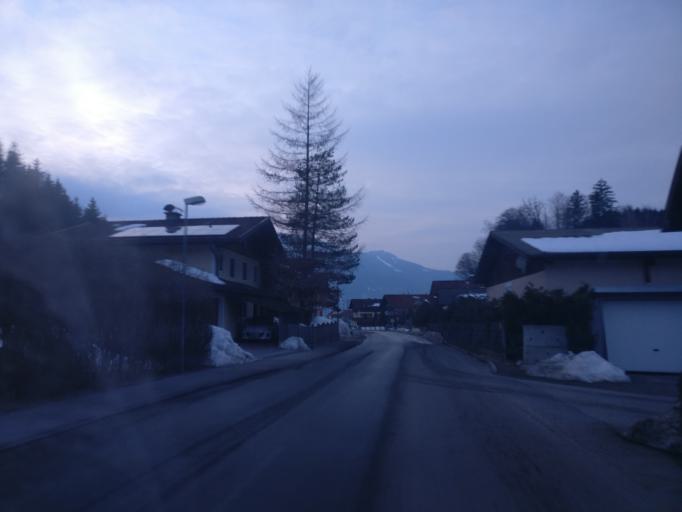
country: AT
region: Salzburg
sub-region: Politischer Bezirk Hallein
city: Golling an der Salzach
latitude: 47.6168
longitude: 13.1731
